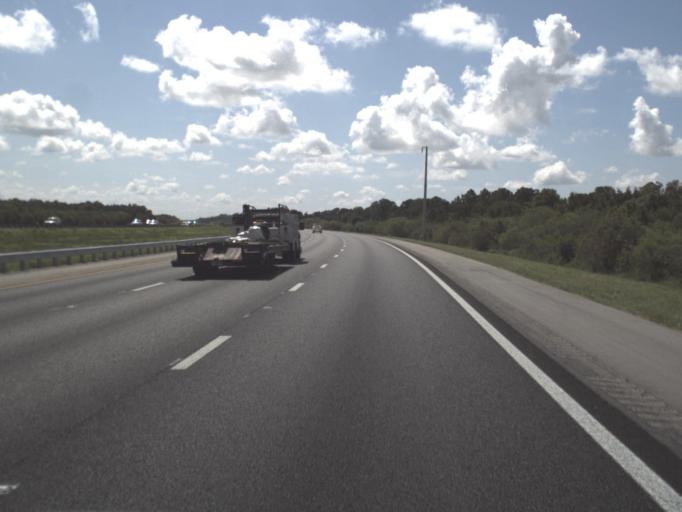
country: US
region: Florida
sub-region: Lee County
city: Suncoast Estates
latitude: 26.7599
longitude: -81.8734
